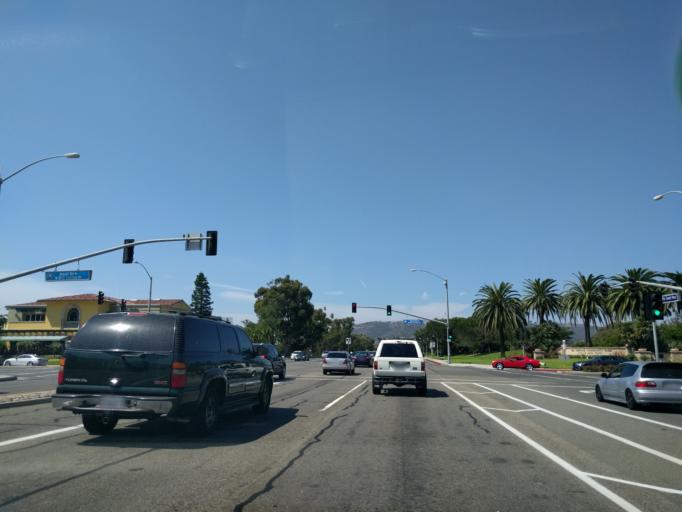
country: US
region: California
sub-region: Orange County
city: Dana Point
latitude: 33.4755
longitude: -117.7164
